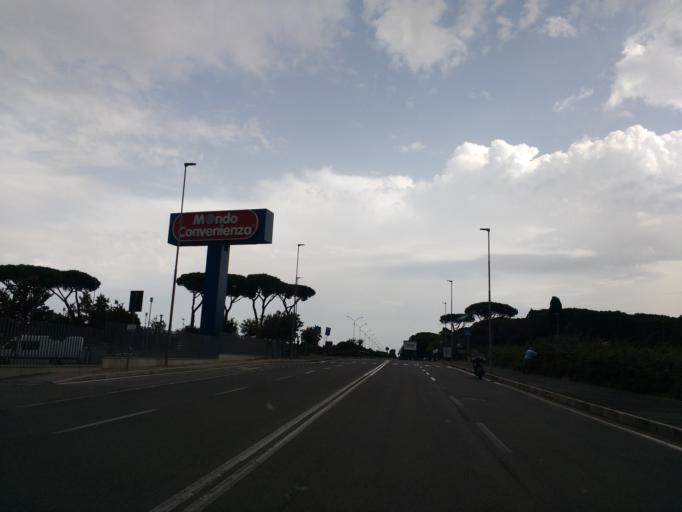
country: IT
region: Latium
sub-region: Citta metropolitana di Roma Capitale
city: Monte Migliore-La Selvotta
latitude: 41.7125
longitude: 12.4449
